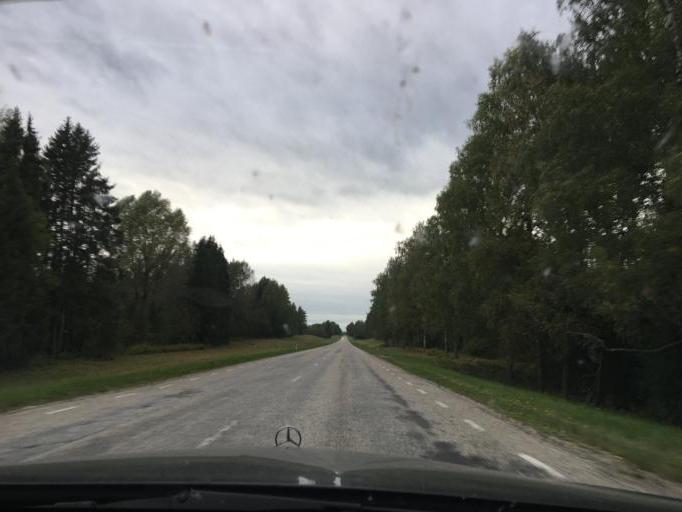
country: LV
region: Aluksnes Rajons
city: Aluksne
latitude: 57.5979
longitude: 27.1967
